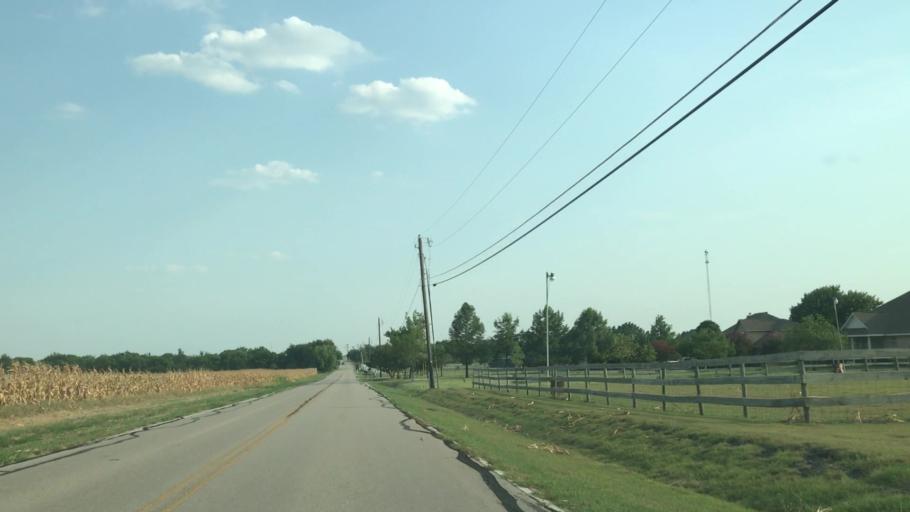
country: US
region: Texas
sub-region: Rockwall County
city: Fate
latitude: 32.9332
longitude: -96.4009
